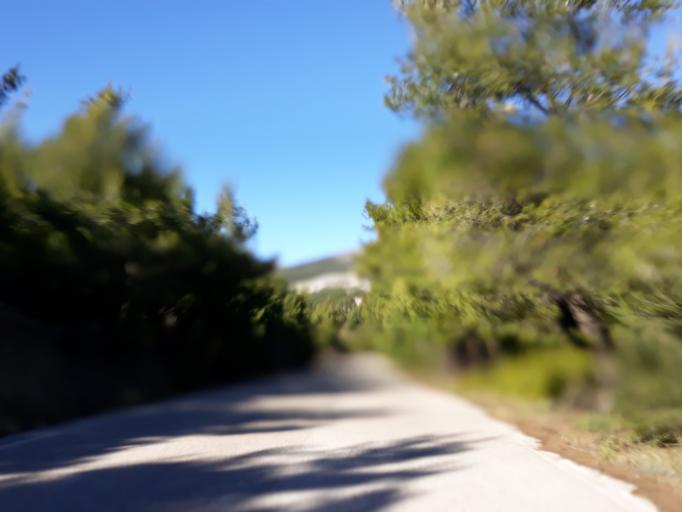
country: GR
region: Attica
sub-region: Nomarchia Dytikis Attikis
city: Fyli
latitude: 38.1268
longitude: 23.6473
